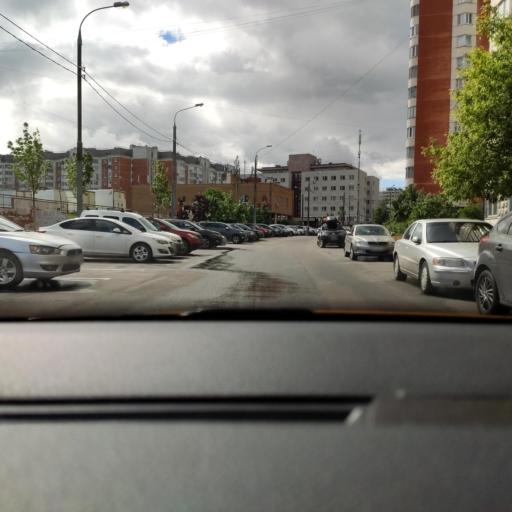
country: RU
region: Moscow
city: Nekrasovka
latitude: 55.7175
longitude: 37.8890
